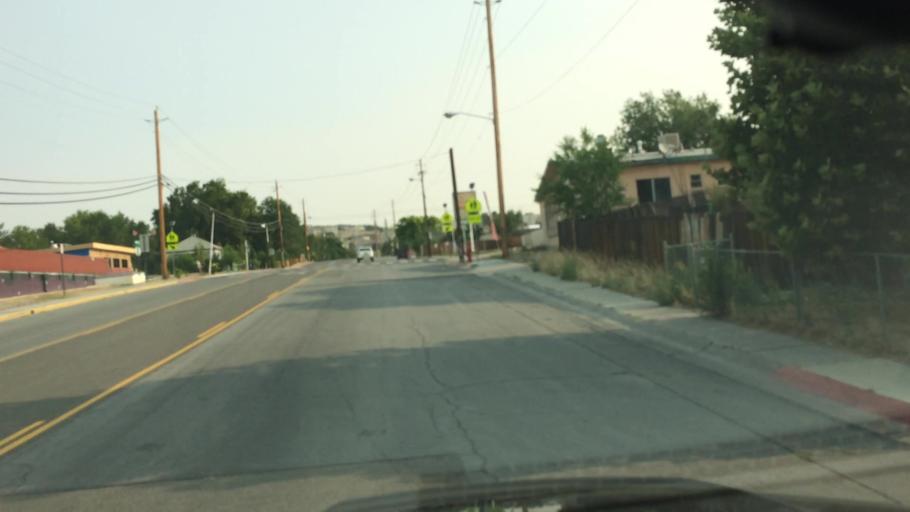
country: US
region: Nevada
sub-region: Washoe County
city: Reno
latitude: 39.5435
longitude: -119.8078
